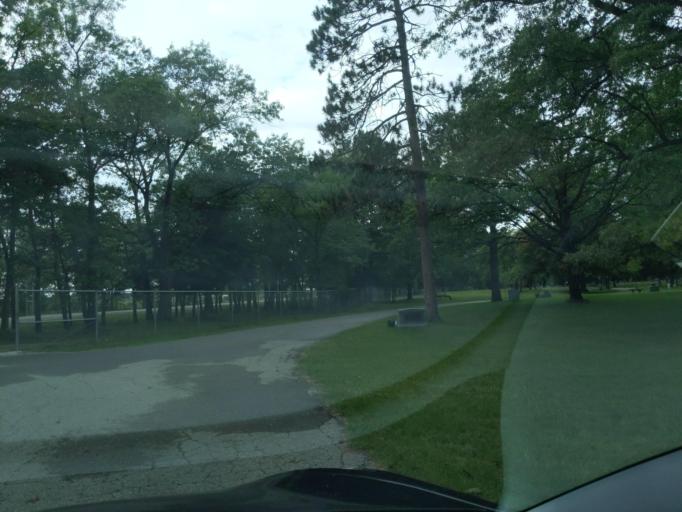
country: US
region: Michigan
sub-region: Grand Traverse County
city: Traverse City
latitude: 44.7526
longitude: -85.5831
